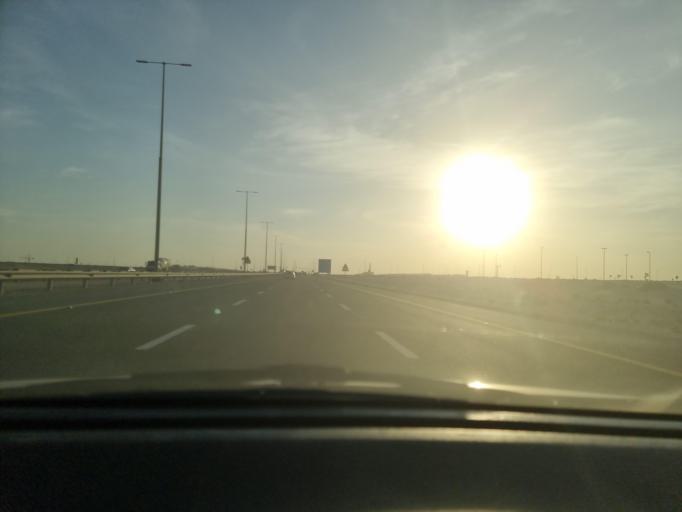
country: AE
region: Abu Dhabi
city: Abu Dhabi
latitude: 24.3417
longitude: 54.7025
